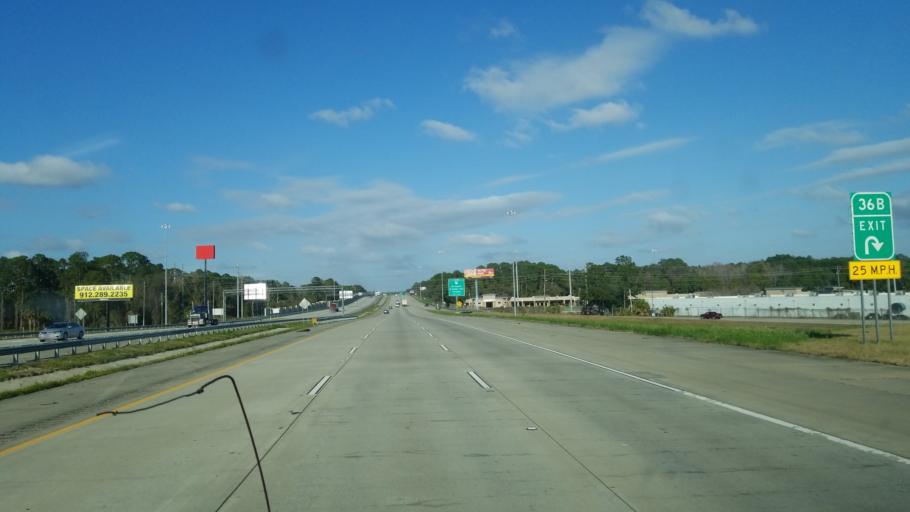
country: US
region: Georgia
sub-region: Glynn County
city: Dock Junction
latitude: 31.2212
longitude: -81.5219
